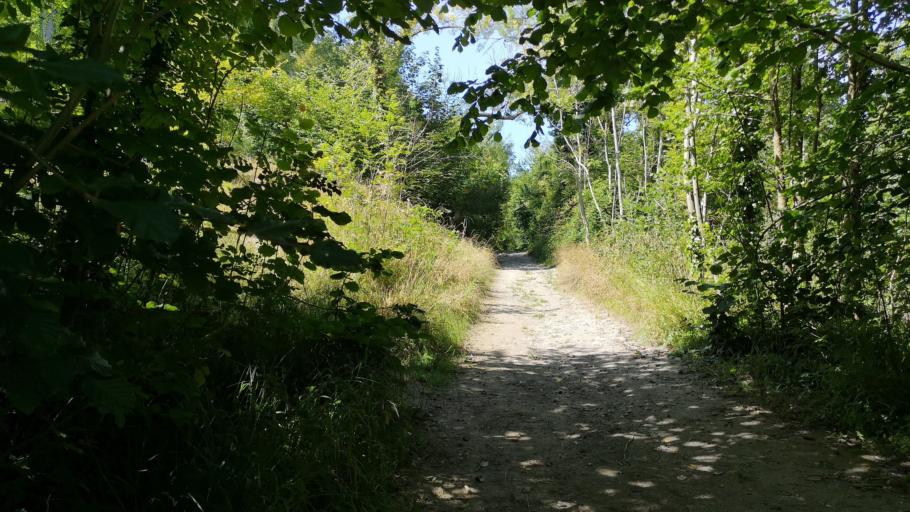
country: GB
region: England
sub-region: Isle of Wight
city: Brading
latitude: 50.6803
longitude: -1.1547
